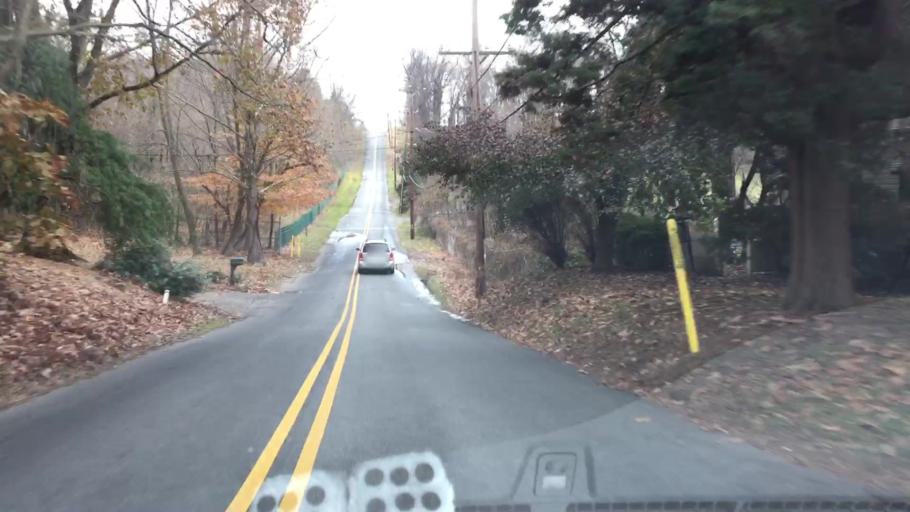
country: US
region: Pennsylvania
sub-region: Delaware County
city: Village Green-Green Ridge
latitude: 39.8711
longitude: -75.4327
